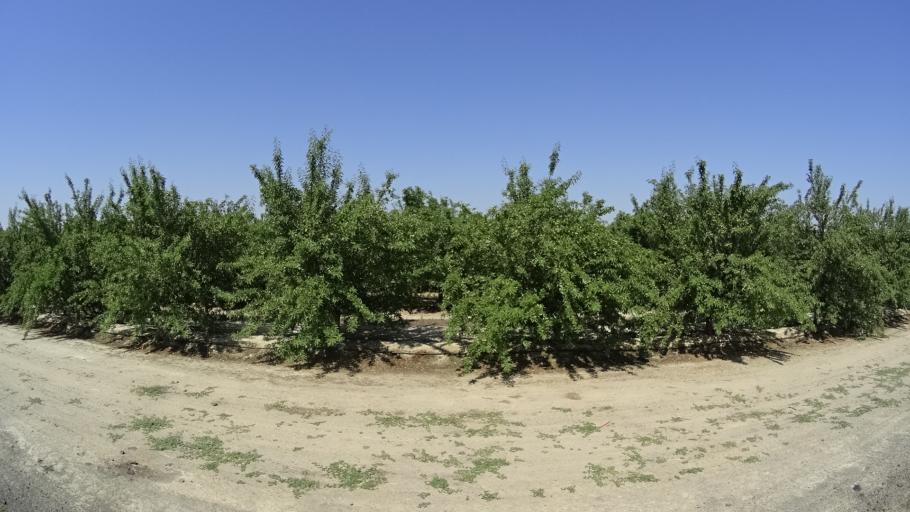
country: US
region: California
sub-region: Fresno County
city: Kingsburg
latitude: 36.4331
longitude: -119.5287
